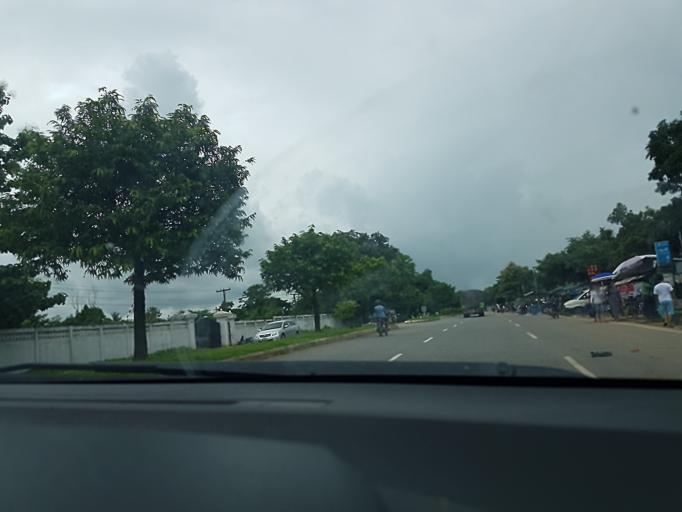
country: MM
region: Bago
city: Thanatpin
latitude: 17.1447
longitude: 96.3083
